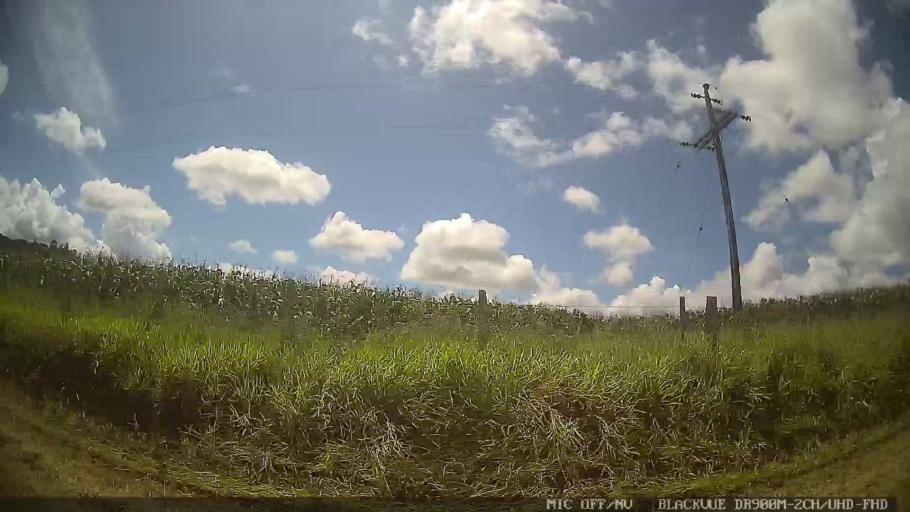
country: BR
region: Sao Paulo
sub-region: Amparo
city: Amparo
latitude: -22.8352
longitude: -46.7044
